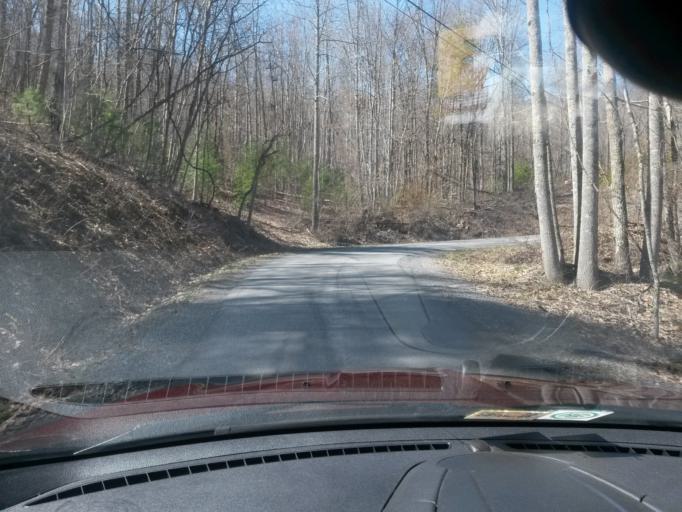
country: US
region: West Virginia
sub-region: Greenbrier County
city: White Sulphur Springs
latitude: 37.6727
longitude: -80.3204
